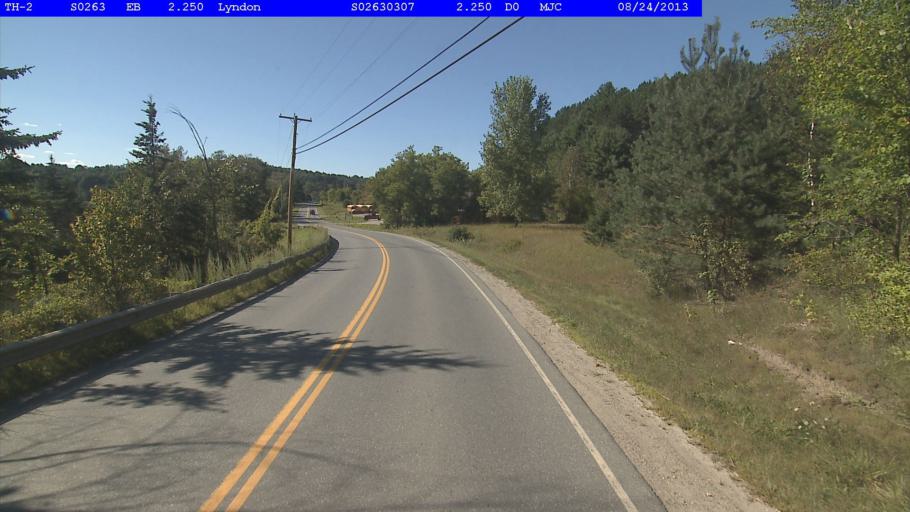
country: US
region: Vermont
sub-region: Caledonia County
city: Lyndon
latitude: 44.5158
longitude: -71.9977
